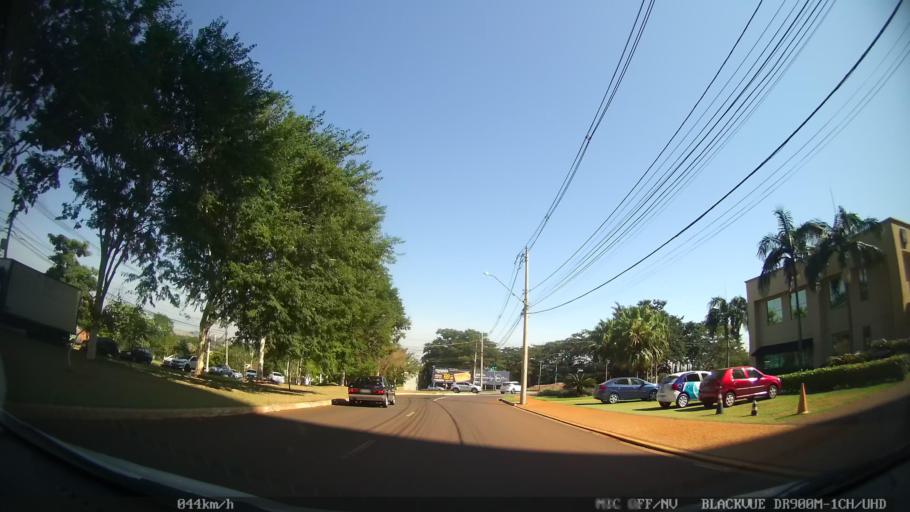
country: BR
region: Sao Paulo
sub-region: Ribeirao Preto
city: Ribeirao Preto
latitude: -21.2194
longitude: -47.8051
